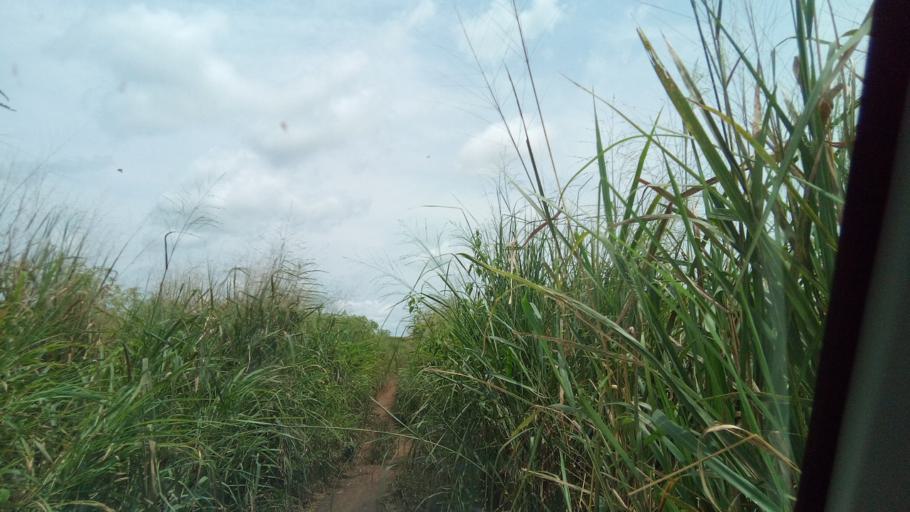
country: AO
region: Zaire
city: Mbanza Congo
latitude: -5.7954
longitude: 13.9949
